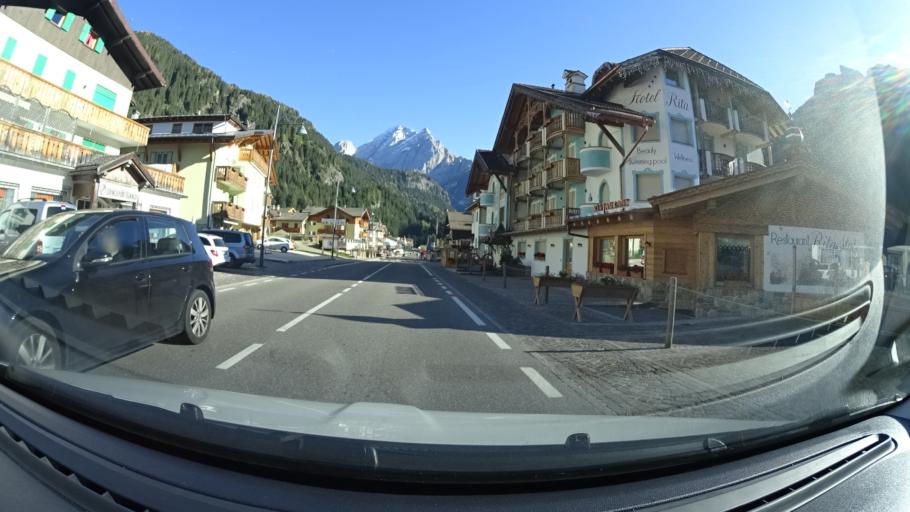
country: IT
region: Trentino-Alto Adige
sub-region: Provincia di Trento
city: Canazei
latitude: 46.4760
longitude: 11.7716
